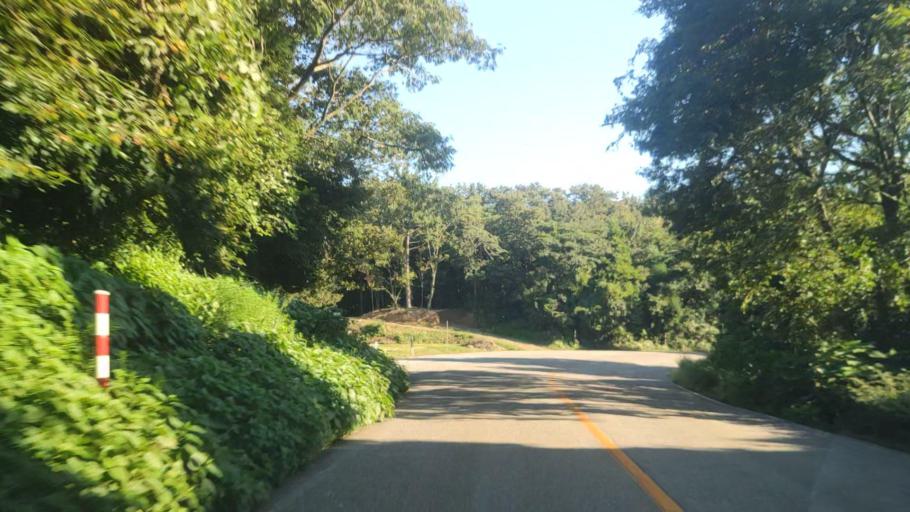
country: JP
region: Ishikawa
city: Nanao
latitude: 37.1027
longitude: 136.9486
